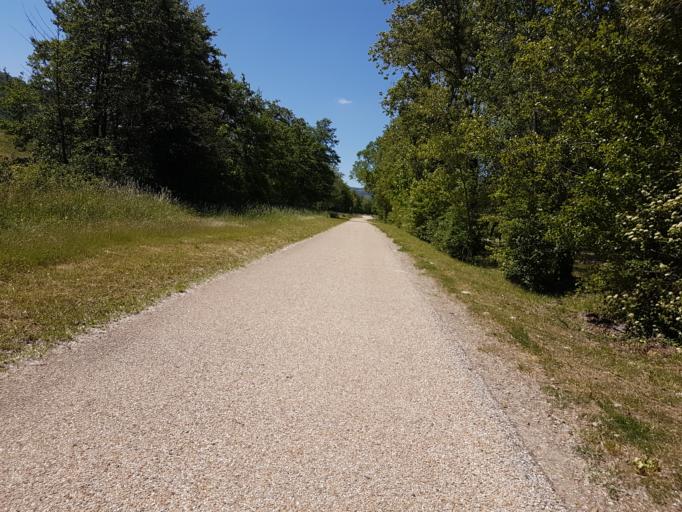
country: FR
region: Rhone-Alpes
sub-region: Departement de la Drome
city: Saint-Vallier
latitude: 45.1528
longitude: 4.8240
